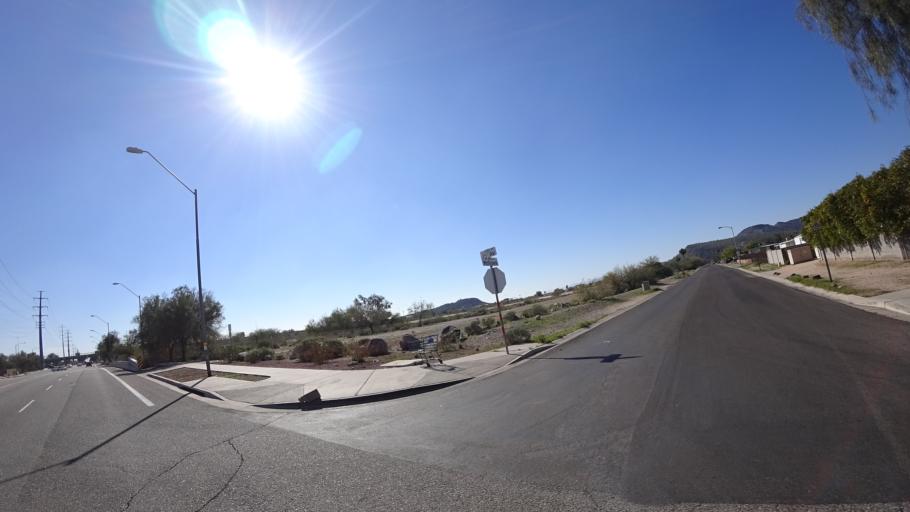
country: US
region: Arizona
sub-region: Maricopa County
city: Peoria
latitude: 33.6730
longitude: -112.1348
